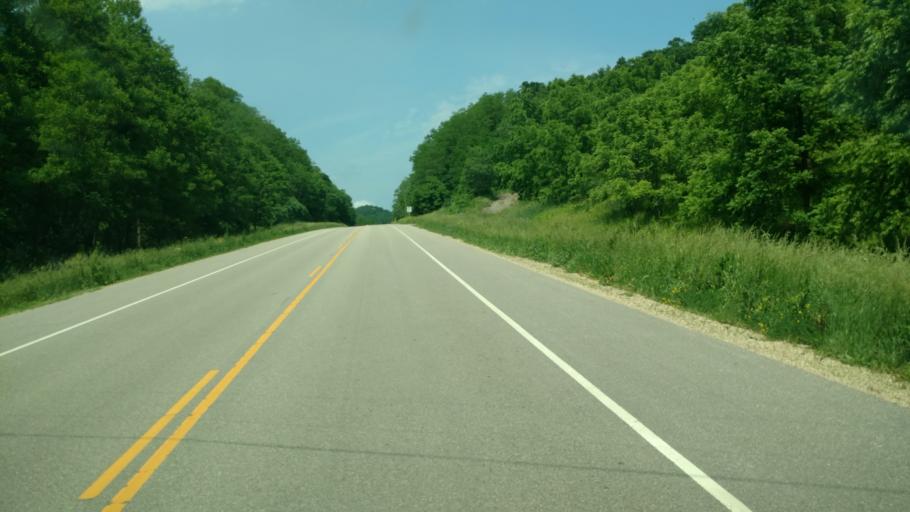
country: US
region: Wisconsin
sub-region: Vernon County
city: Westby
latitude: 43.5502
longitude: -90.6647
